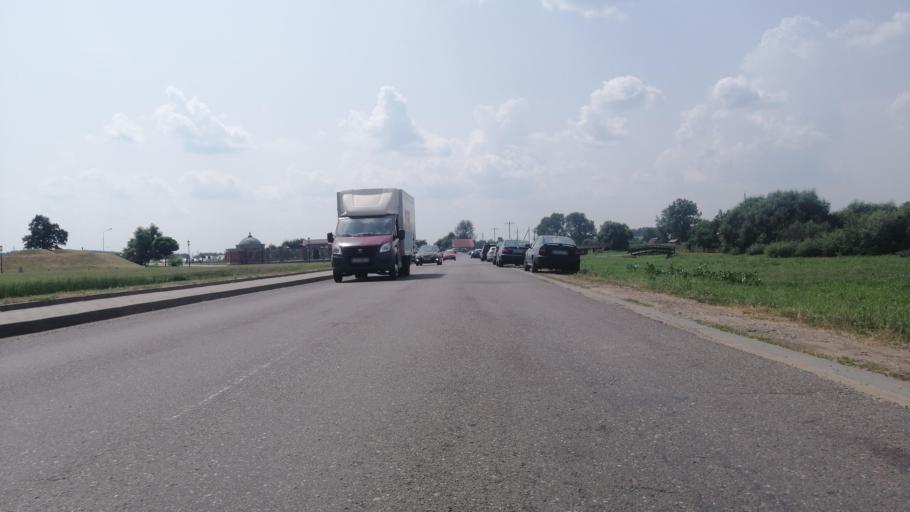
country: BY
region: Grodnenskaya
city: Mir
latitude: 53.4534
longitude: 26.4723
